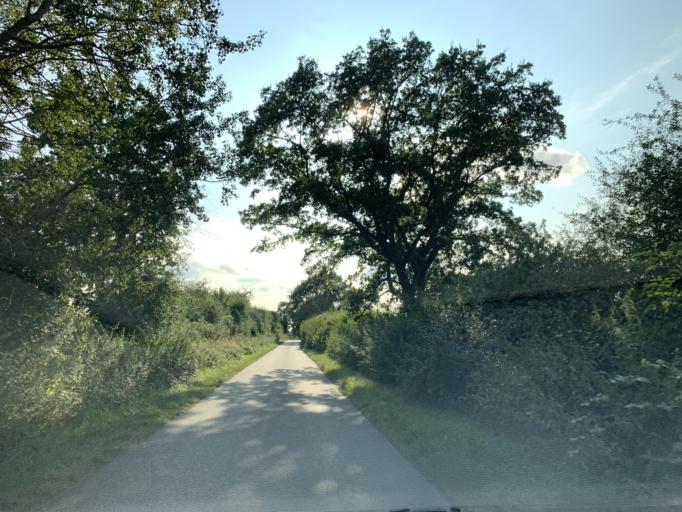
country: DE
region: Mecklenburg-Vorpommern
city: Loitz
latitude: 53.3553
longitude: 13.3713
